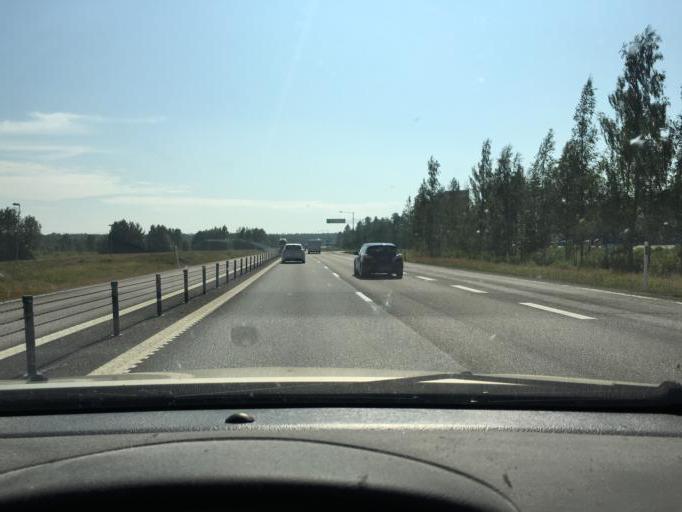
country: SE
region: Norrbotten
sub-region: Lulea Kommun
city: Gammelstad
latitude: 65.6166
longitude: 22.0567
